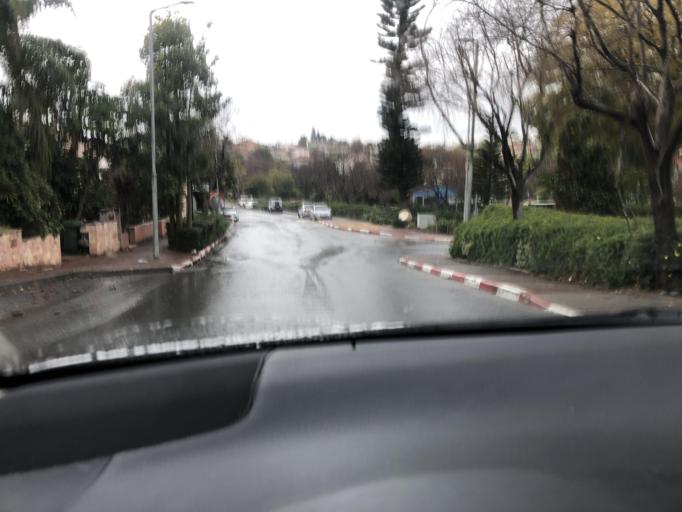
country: PS
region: West Bank
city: Azun Atme
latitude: 32.1115
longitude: 35.0298
